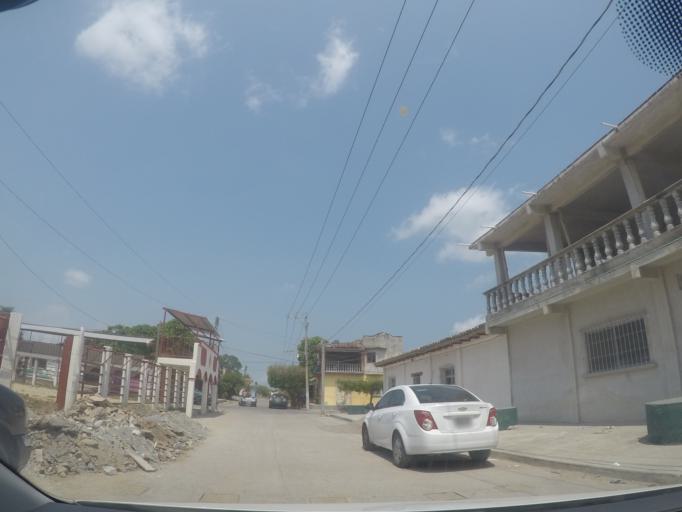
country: MX
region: Oaxaca
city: Asuncion Ixtaltepec
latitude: 16.5031
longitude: -95.0579
